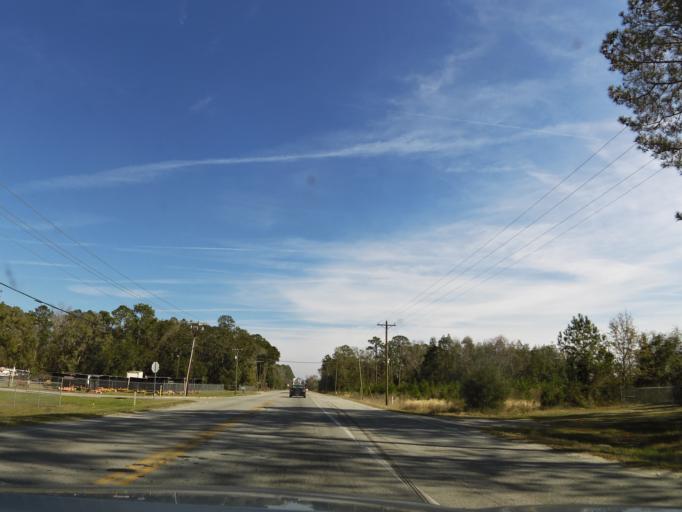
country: US
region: Georgia
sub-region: Glynn County
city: Dock Junction
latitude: 31.2724
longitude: -81.5528
